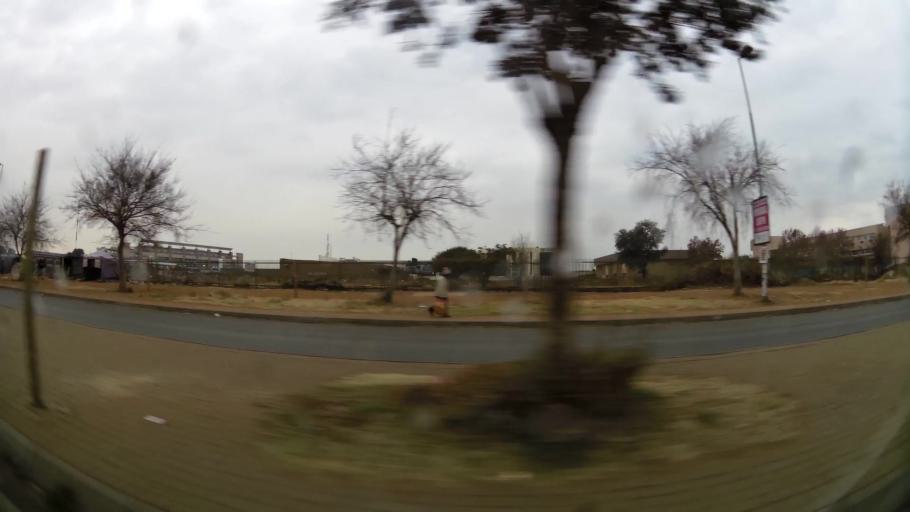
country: ZA
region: Gauteng
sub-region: City of Johannesburg Metropolitan Municipality
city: Soweto
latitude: -26.2498
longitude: 27.8539
